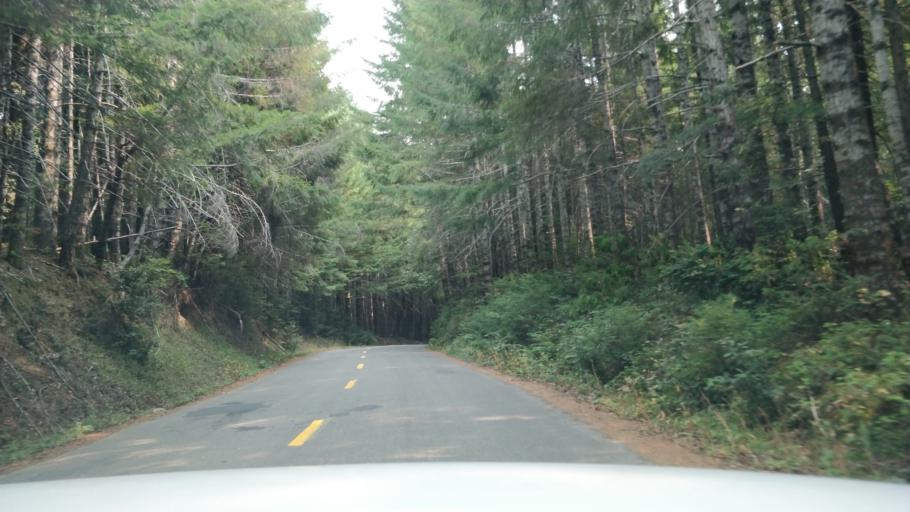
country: US
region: California
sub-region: Humboldt County
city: Westhaven-Moonstone
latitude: 41.2497
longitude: -123.9852
